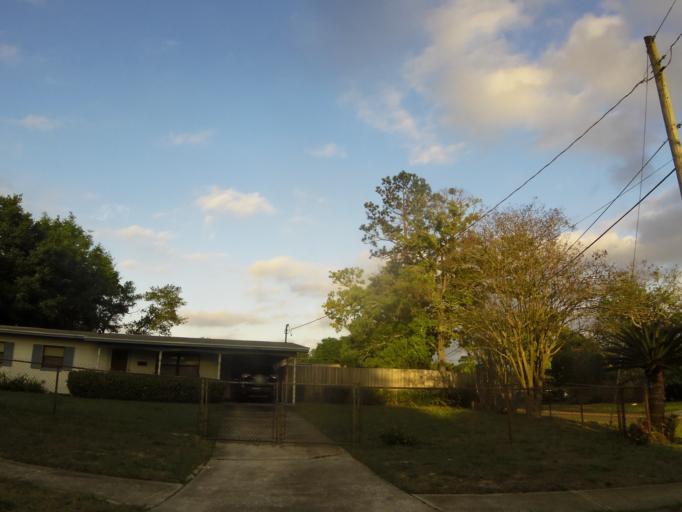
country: US
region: Florida
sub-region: Duval County
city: Jacksonville
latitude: 30.4434
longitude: -81.6297
